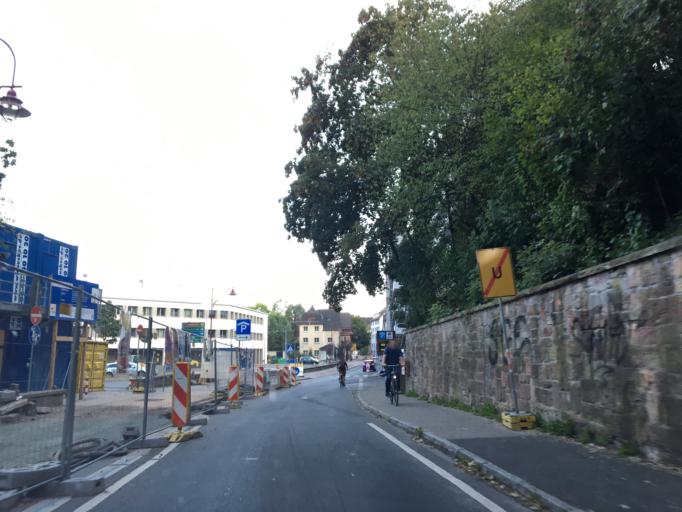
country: DE
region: Hesse
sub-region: Regierungsbezirk Giessen
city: Marburg an der Lahn
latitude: 50.8117
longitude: 8.7713
